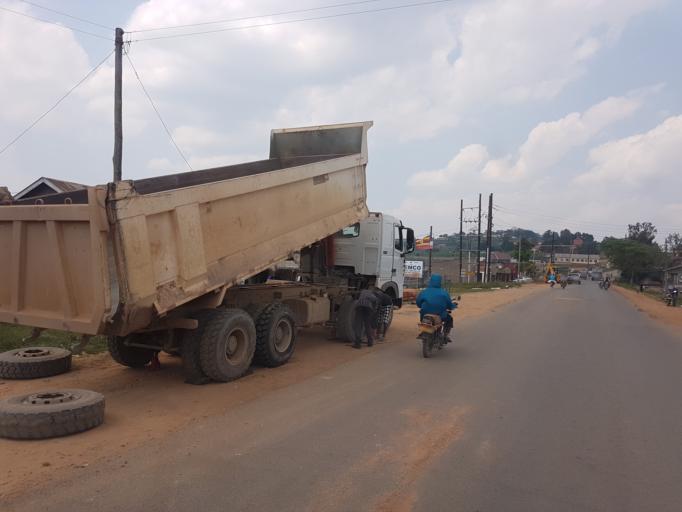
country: UG
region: Western Region
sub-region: Bushenyi District
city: Bushenyi
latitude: -0.5401
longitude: 30.1288
